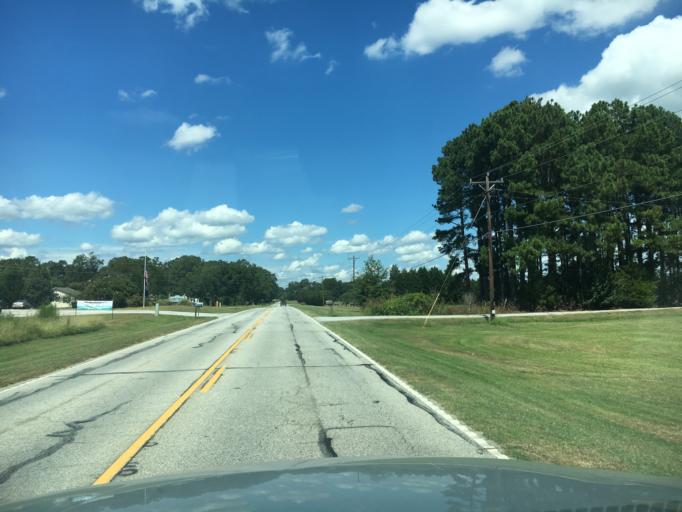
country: US
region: South Carolina
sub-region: Laurens County
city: Laurens
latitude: 34.5032
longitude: -82.0747
